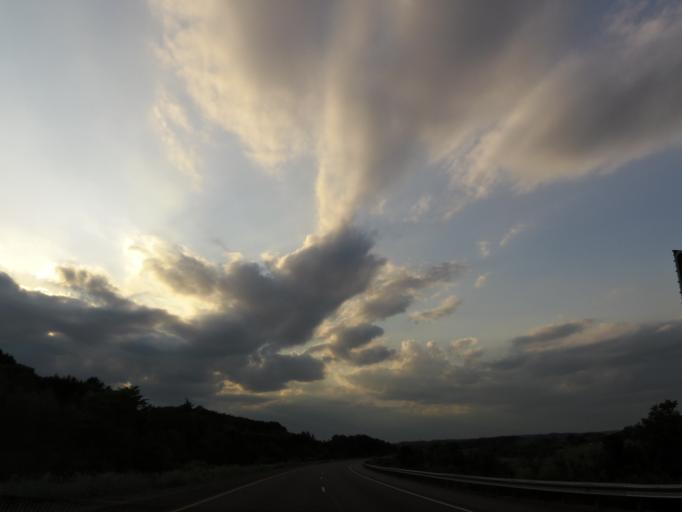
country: US
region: Wisconsin
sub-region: Trempealeau County
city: Osseo
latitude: 44.4422
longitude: -91.0771
